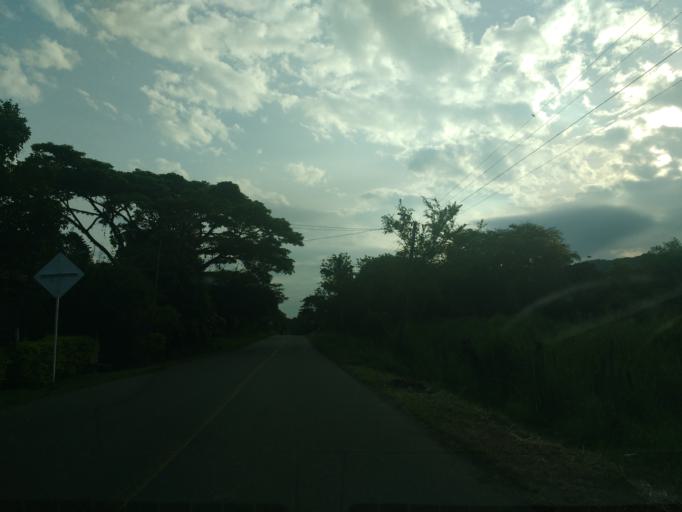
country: CO
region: Cauca
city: Caloto
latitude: 3.0741
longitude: -76.3515
